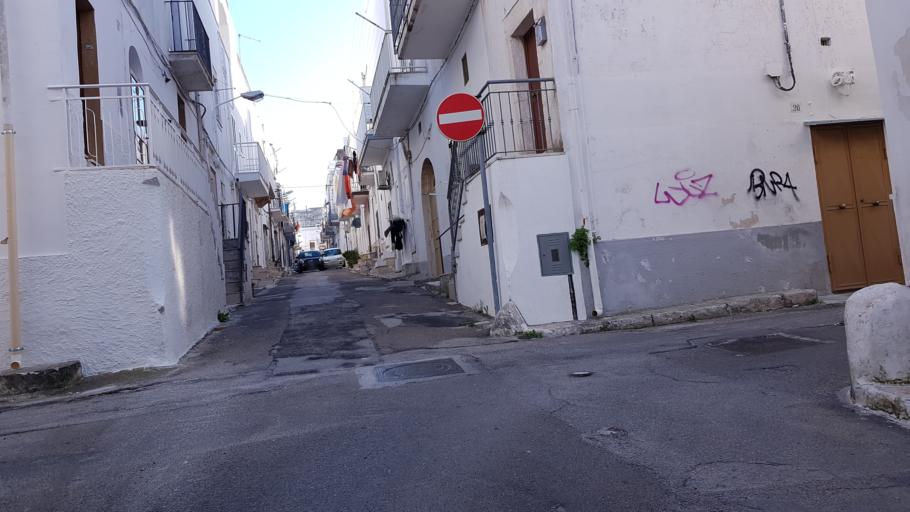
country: IT
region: Apulia
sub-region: Provincia di Brindisi
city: Ostuni
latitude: 40.7292
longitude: 17.5809
